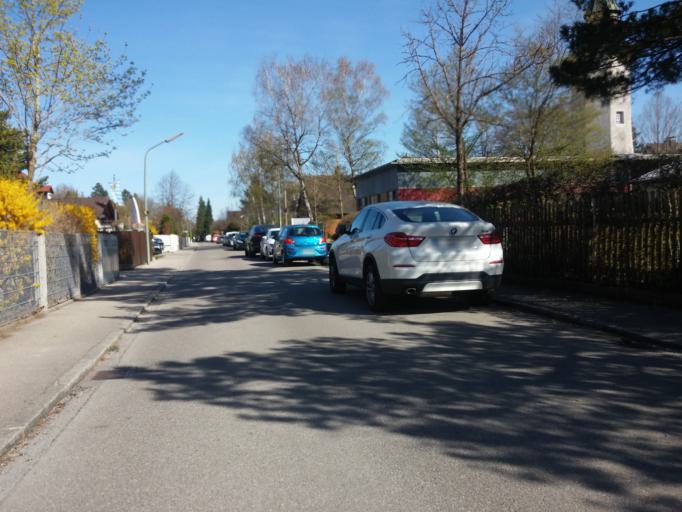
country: DE
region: Bavaria
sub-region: Upper Bavaria
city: Neubiberg
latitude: 48.0808
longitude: 11.6745
